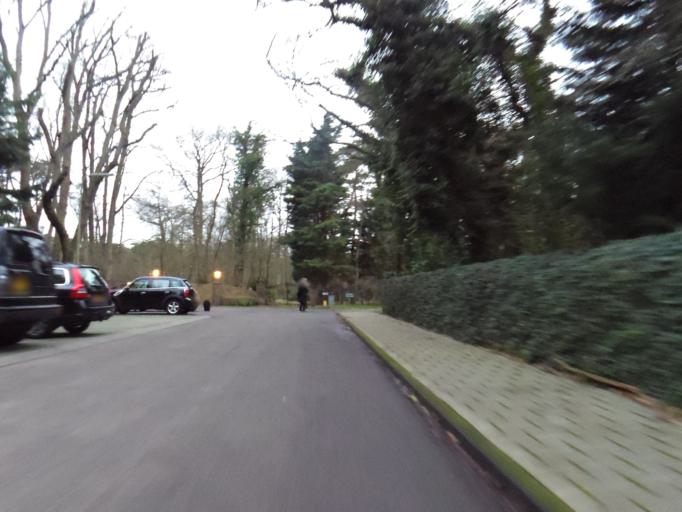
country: NL
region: North Holland
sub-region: Gemeente Bloemendaal
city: Bennebroek
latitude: 52.3551
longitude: 4.5780
